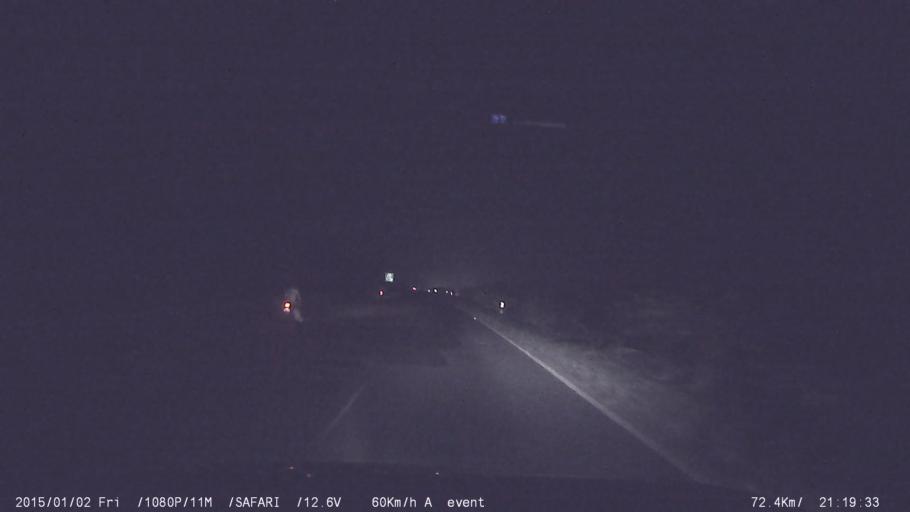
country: IN
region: Tamil Nadu
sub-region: Kancheepuram
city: Kanchipuram
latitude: 12.8774
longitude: 79.6124
